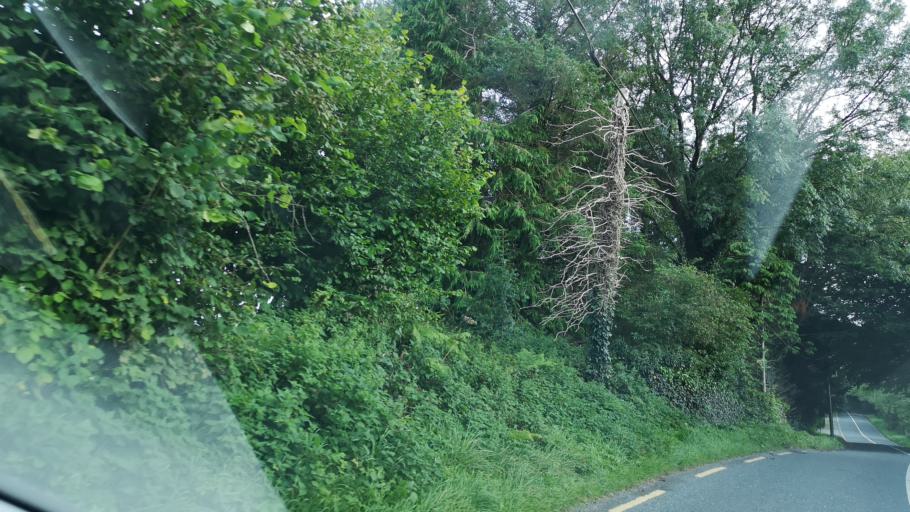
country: IE
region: Connaught
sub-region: County Galway
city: Ballinasloe
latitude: 53.3214
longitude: -8.2788
